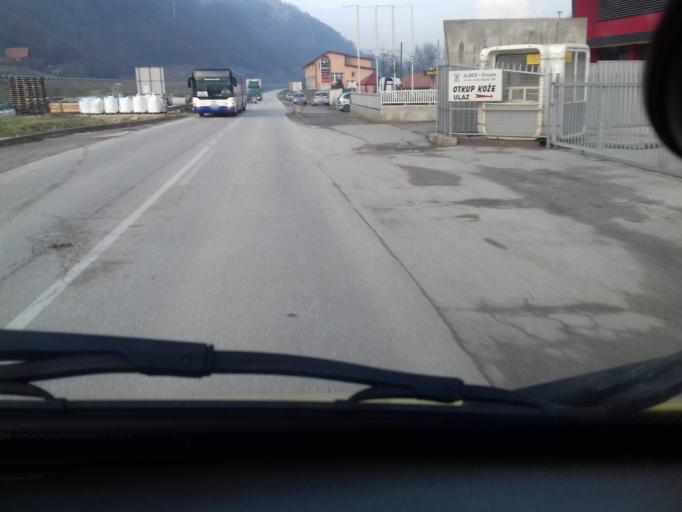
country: BA
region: Federation of Bosnia and Herzegovina
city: Dobrinje
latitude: 44.0558
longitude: 18.1040
